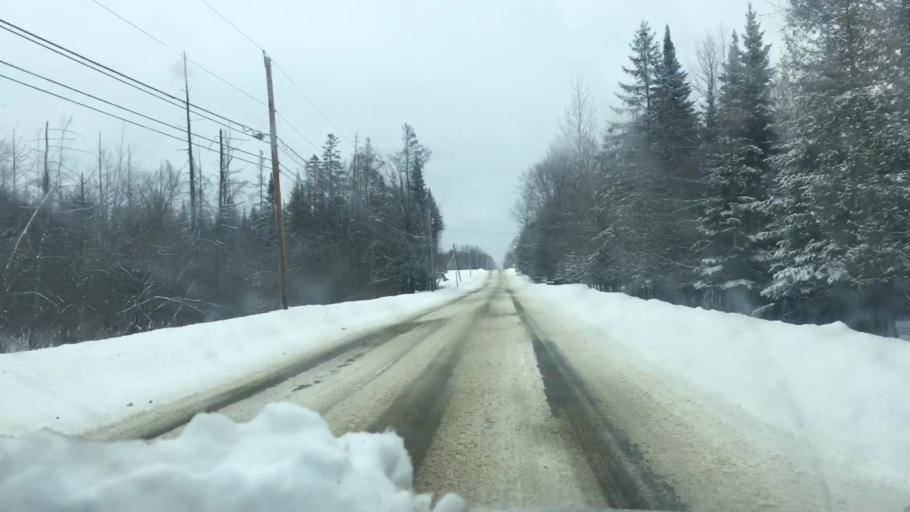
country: US
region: Maine
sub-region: Penobscot County
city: Bradford
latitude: 45.0120
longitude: -68.9918
